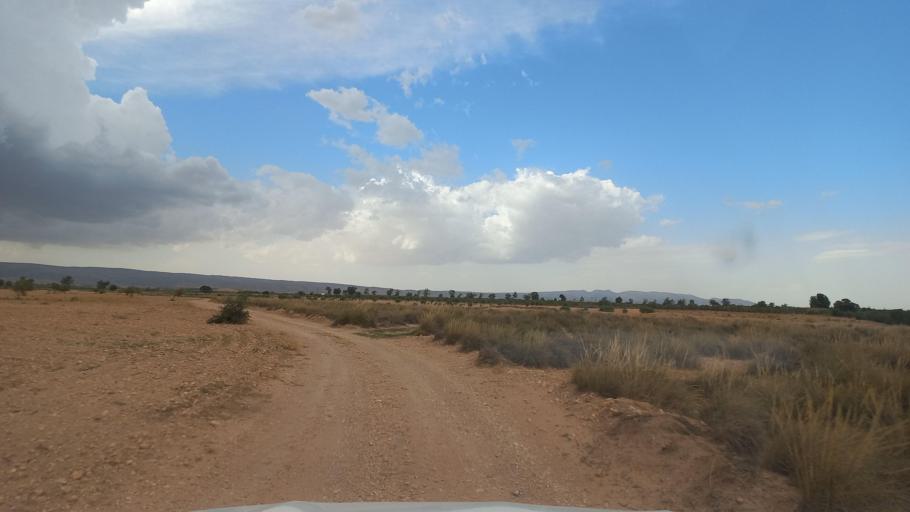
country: TN
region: Al Qasrayn
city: Kasserine
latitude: 35.2431
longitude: 9.0087
